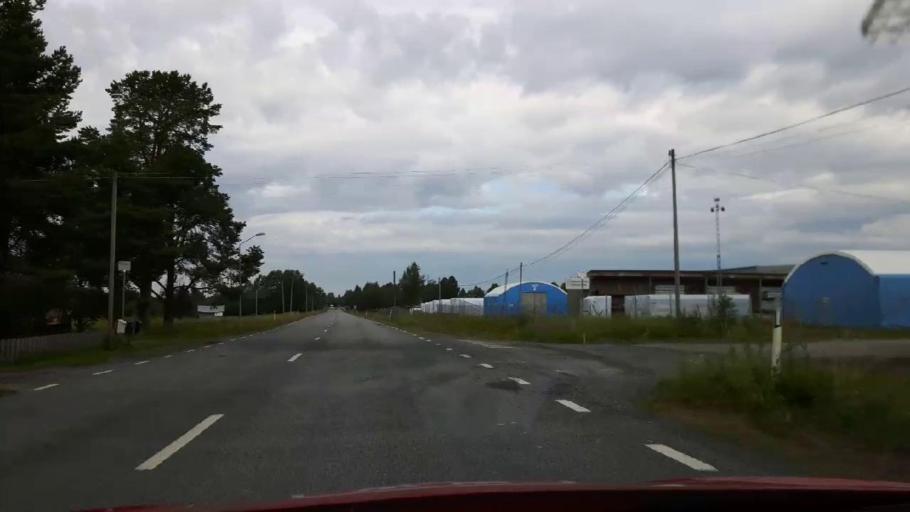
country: SE
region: Jaemtland
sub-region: Stroemsunds Kommun
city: Stroemsund
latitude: 63.5707
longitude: 15.3609
